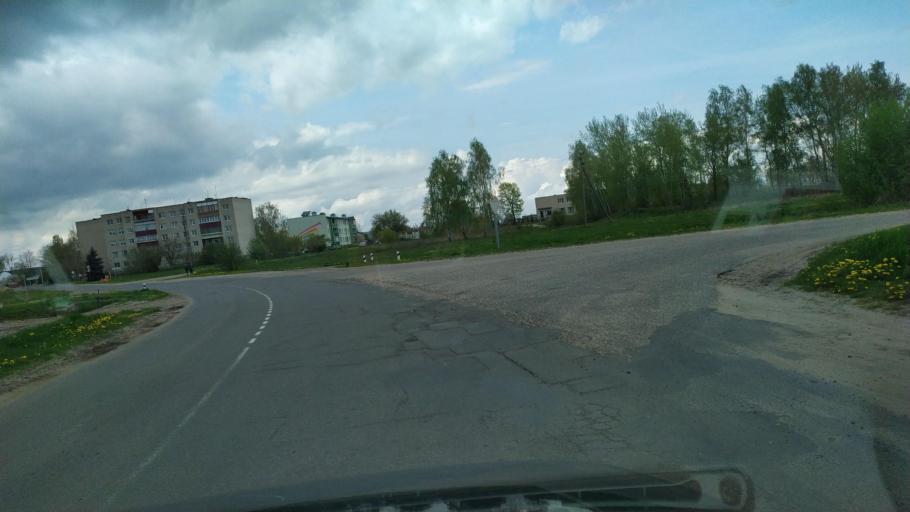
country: BY
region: Brest
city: Pruzhany
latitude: 52.5639
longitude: 24.4229
